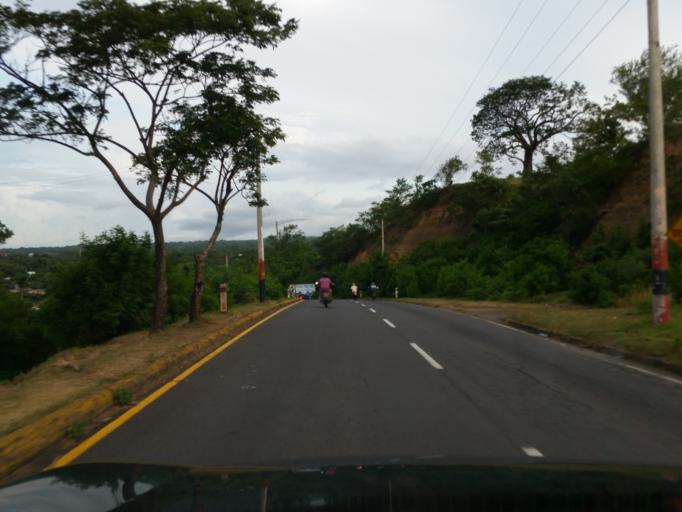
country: NI
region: Managua
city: Managua
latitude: 12.1088
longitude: -86.3025
